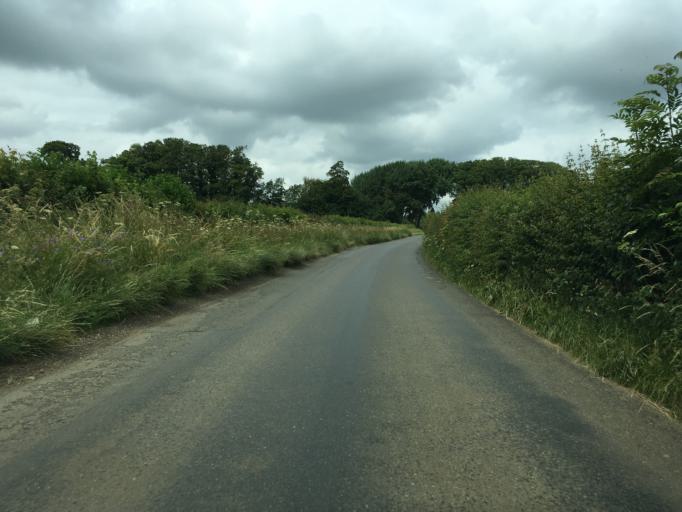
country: GB
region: England
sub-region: Oxfordshire
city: Bloxham
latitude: 51.9530
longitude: -1.4069
